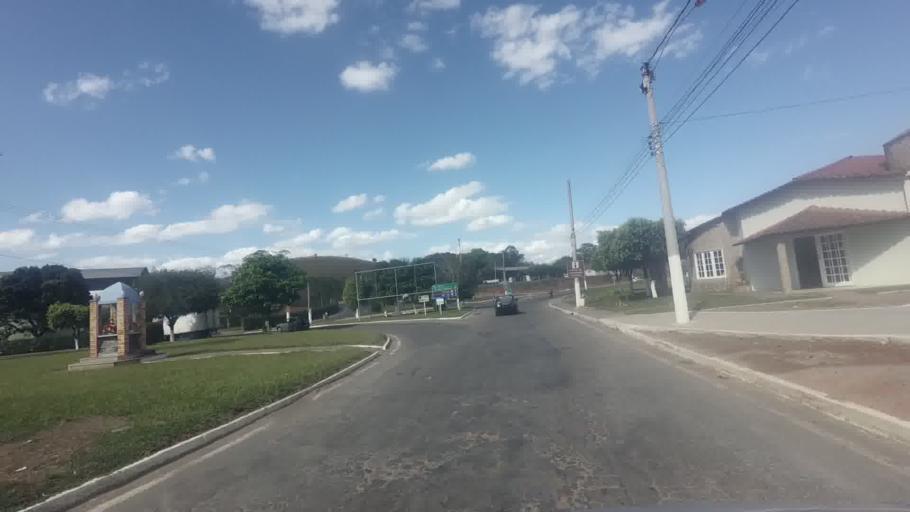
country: BR
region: Rio de Janeiro
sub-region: Bom Jesus Do Itabapoana
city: Bom Jesus do Itabapoana
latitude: -21.1357
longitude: -41.6623
